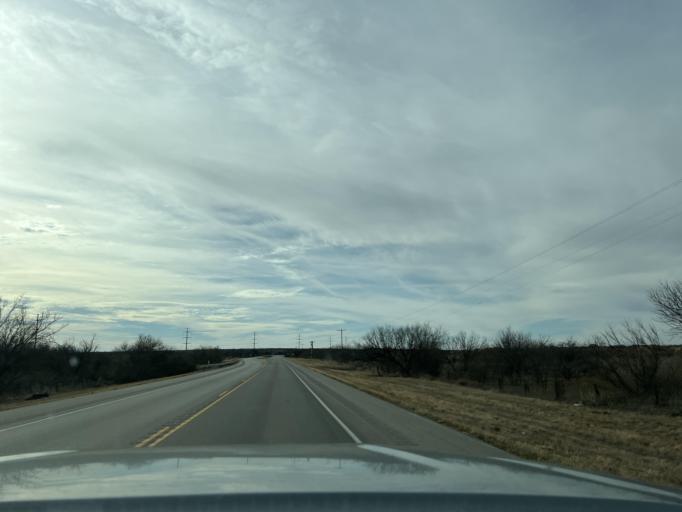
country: US
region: Texas
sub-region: Jones County
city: Stamford
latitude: 32.7540
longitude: -99.6185
